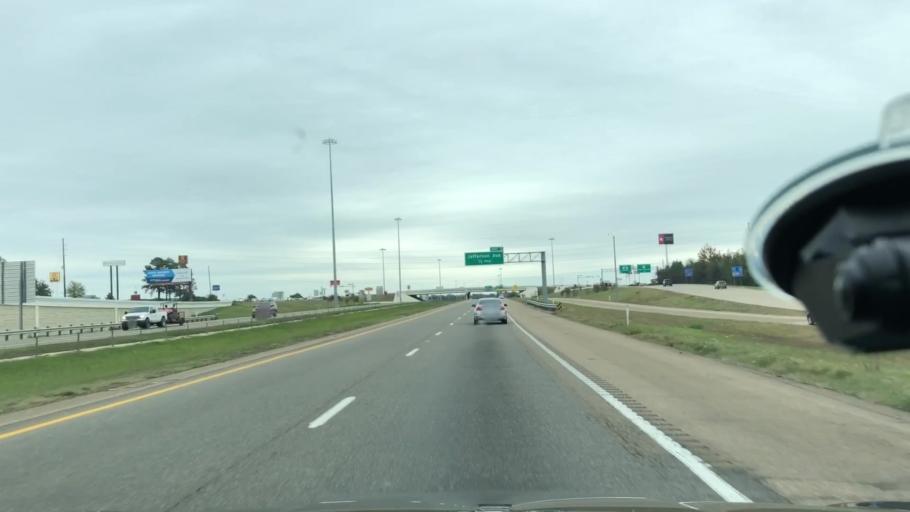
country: US
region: Arkansas
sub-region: Miller County
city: Texarkana
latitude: 33.4701
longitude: -94.0486
